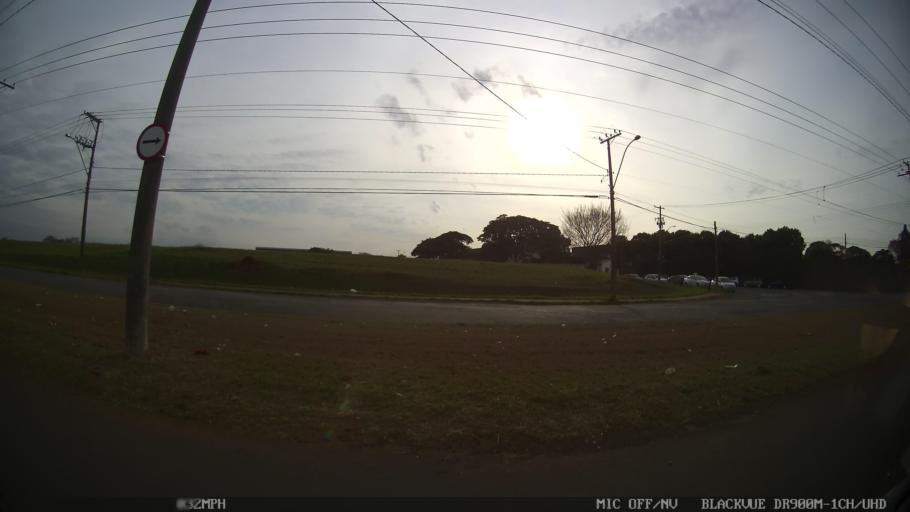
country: BR
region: Sao Paulo
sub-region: Piracicaba
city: Piracicaba
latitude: -22.7321
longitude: -47.5877
